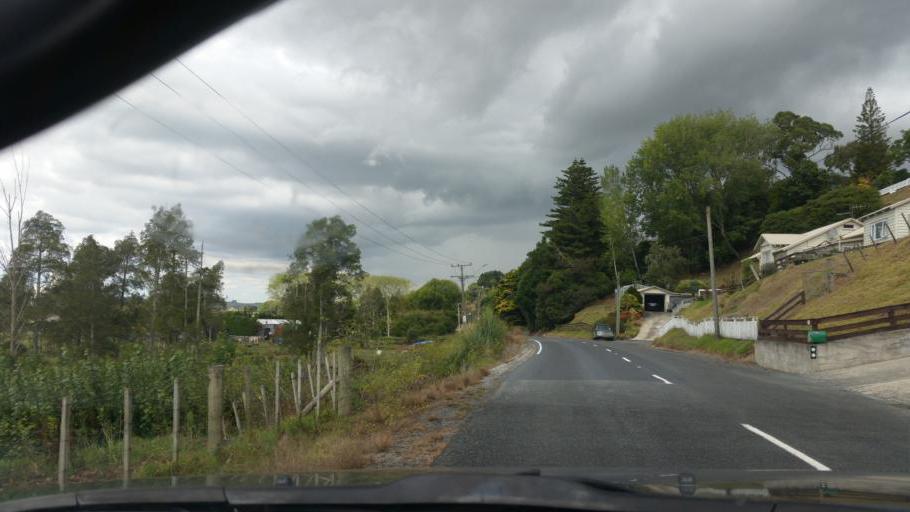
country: NZ
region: Northland
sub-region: Kaipara District
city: Dargaville
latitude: -35.9530
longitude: 173.8572
